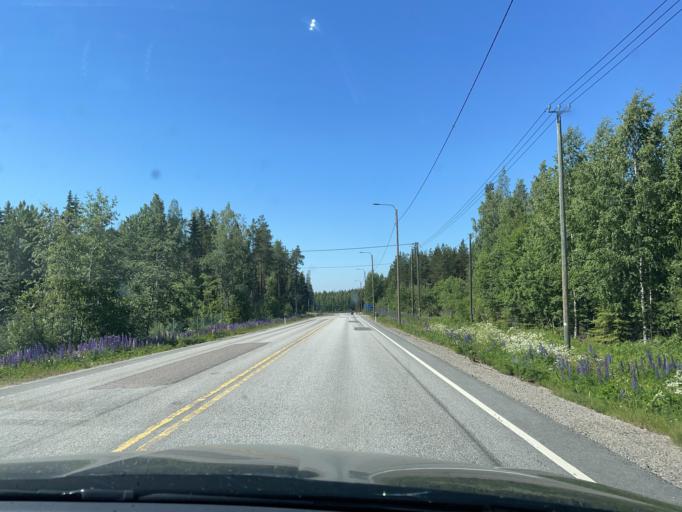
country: FI
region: Central Finland
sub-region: Saarijaervi-Viitasaari
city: Viitasaari
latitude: 63.1391
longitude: 25.7758
